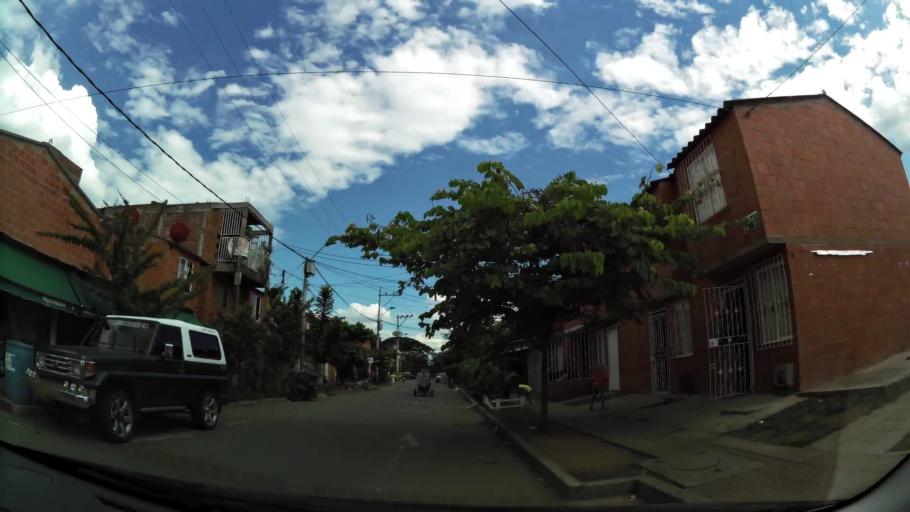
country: CO
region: Valle del Cauca
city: Cali
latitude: 3.3911
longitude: -76.5085
